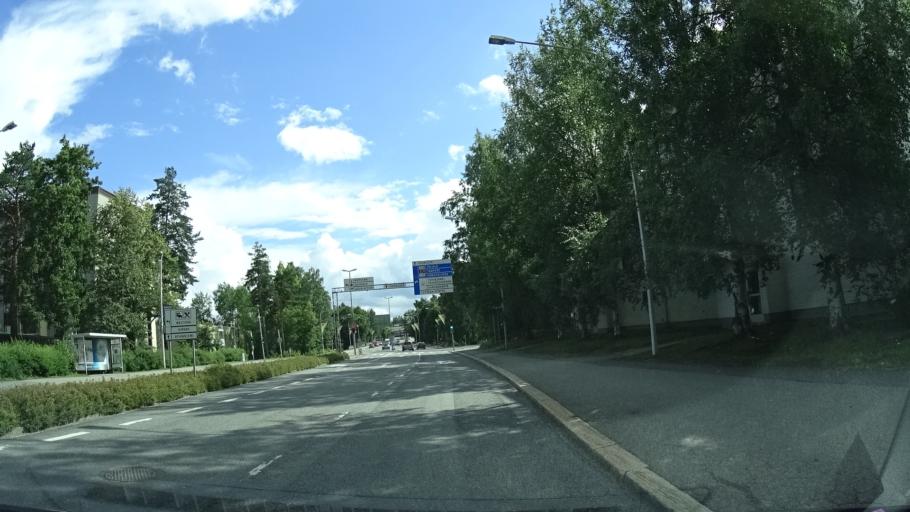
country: FI
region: Pirkanmaa
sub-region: Etelae-Pirkanmaa
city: Valkeakoski
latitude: 61.2719
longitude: 24.0212
